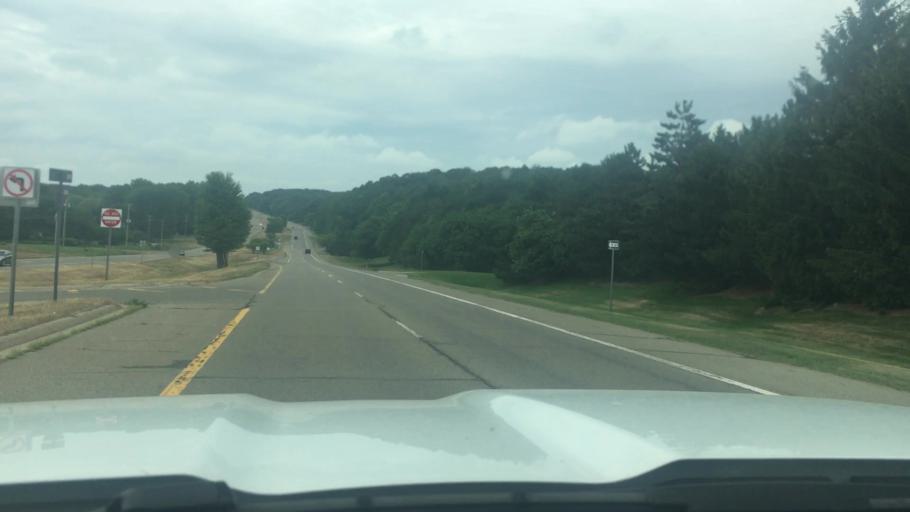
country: US
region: Michigan
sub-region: Kent County
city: Forest Hills
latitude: 42.9626
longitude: -85.5127
